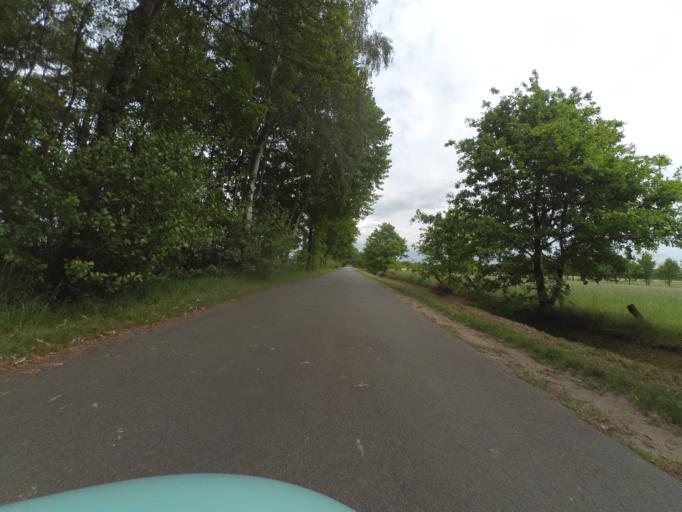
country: DE
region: Lower Saxony
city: Langenhagen
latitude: 52.4703
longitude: 9.7062
